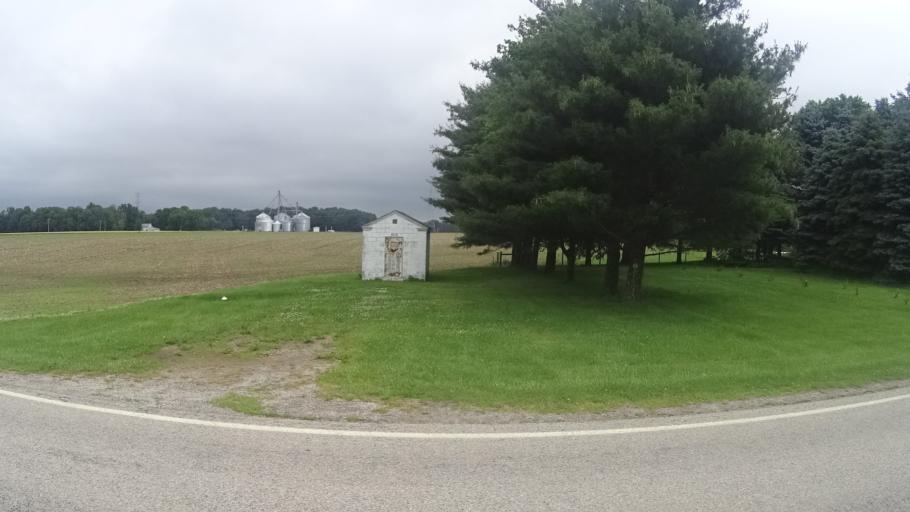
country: US
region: Ohio
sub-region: Erie County
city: Huron
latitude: 41.3306
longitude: -82.5173
